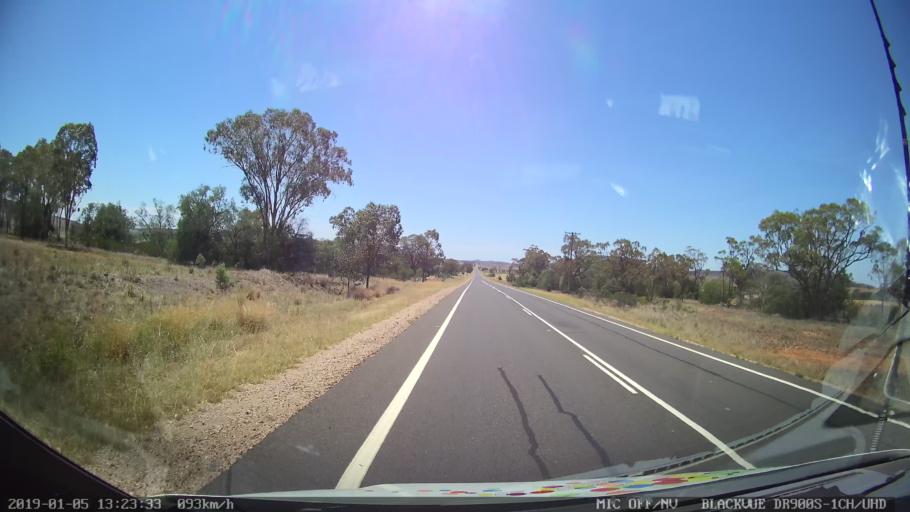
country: AU
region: New South Wales
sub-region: Gunnedah
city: Gunnedah
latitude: -31.0770
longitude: 149.9767
